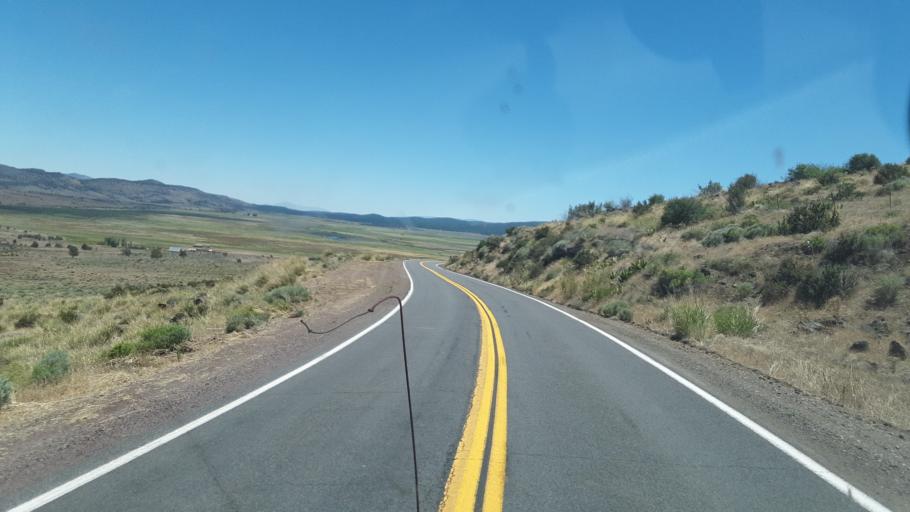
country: US
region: California
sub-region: Lassen County
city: Susanville
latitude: 40.5922
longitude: -120.6435
